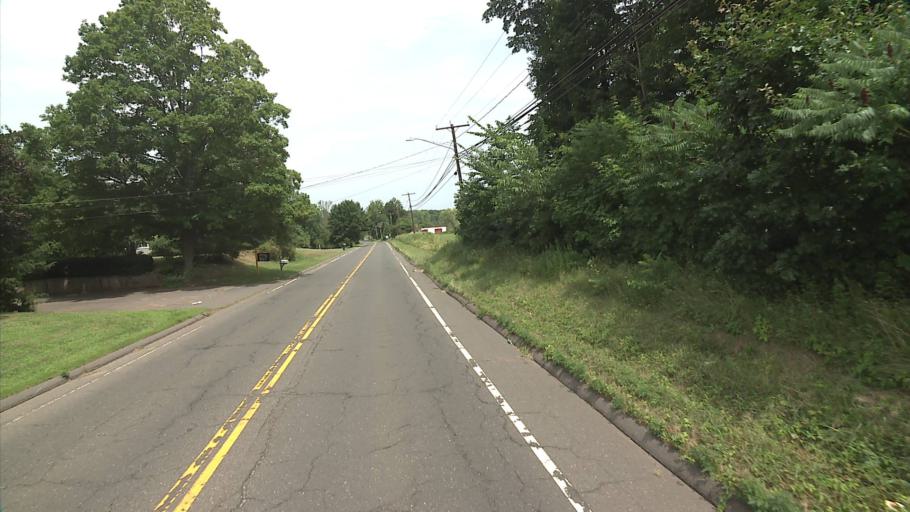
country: US
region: Connecticut
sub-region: Hartford County
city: Kensington
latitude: 41.5997
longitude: -72.7982
